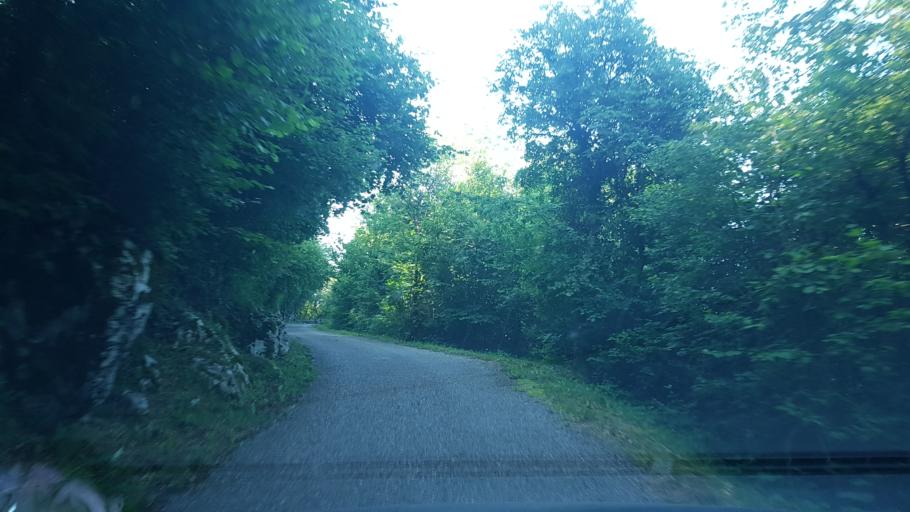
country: IT
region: Friuli Venezia Giulia
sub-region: Provincia di Udine
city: Nimis
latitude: 46.2320
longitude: 13.2520
